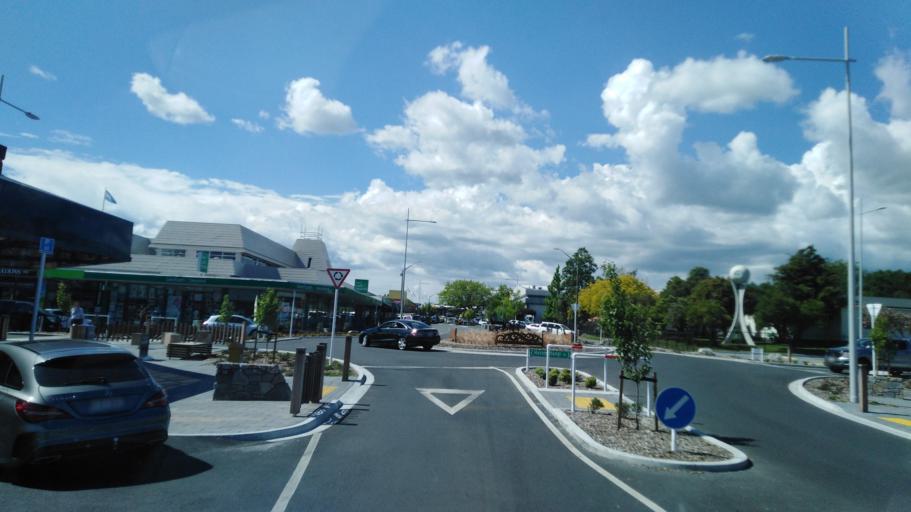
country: NZ
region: Waikato
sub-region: Taupo District
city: Taupo
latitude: -38.6878
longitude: 176.0722
